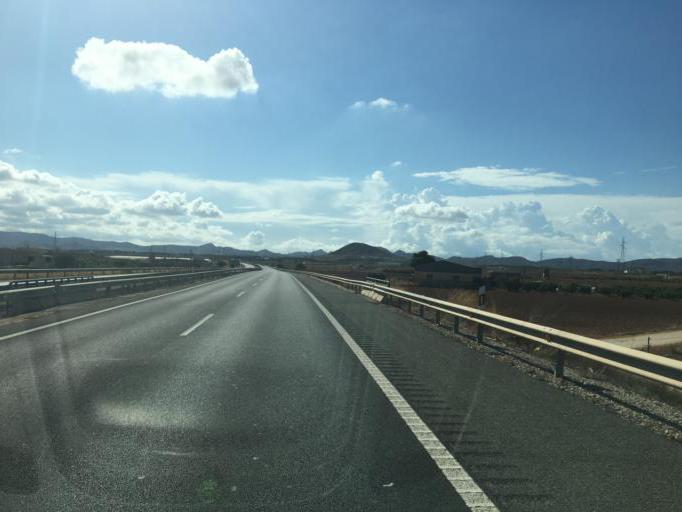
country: ES
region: Murcia
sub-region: Murcia
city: Cartagena
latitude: 37.6493
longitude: -0.9738
